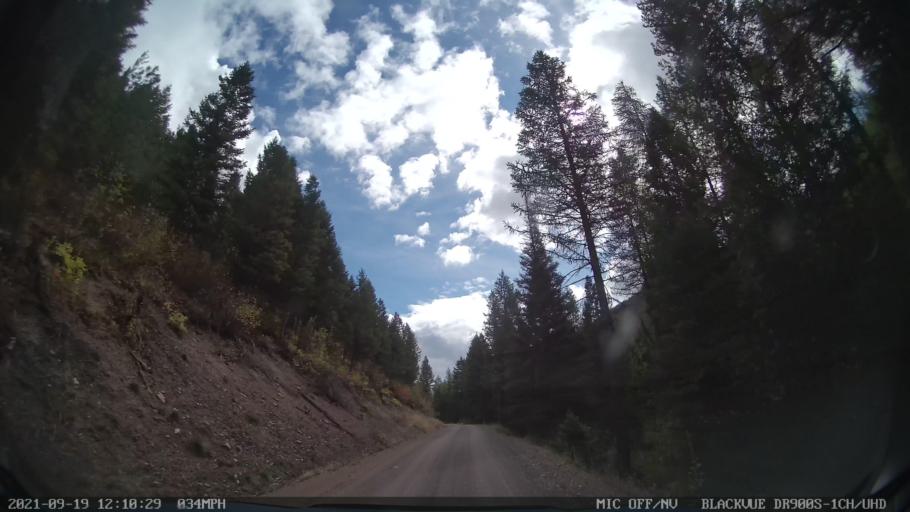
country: US
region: Montana
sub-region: Missoula County
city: Seeley Lake
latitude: 47.1786
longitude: -113.3829
